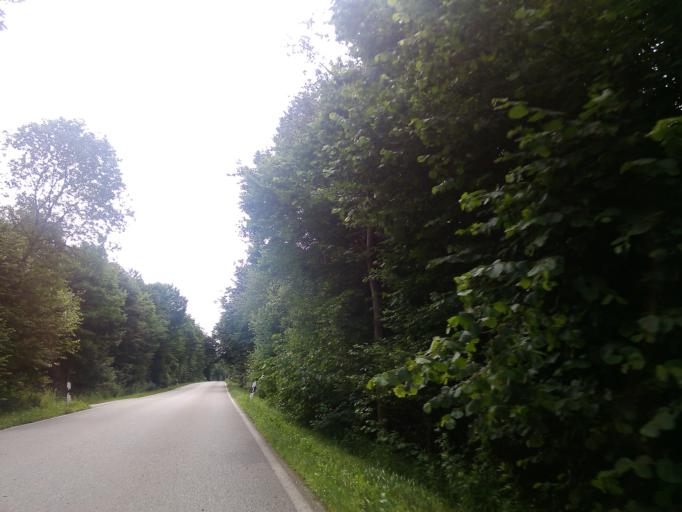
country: DE
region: Bavaria
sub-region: Upper Bavaria
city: Gauting
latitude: 48.0785
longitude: 11.3553
